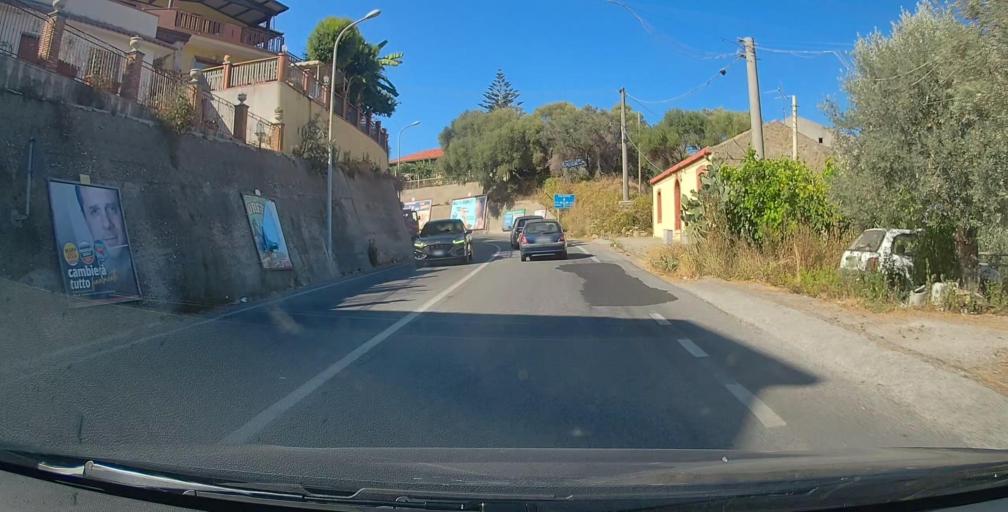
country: IT
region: Sicily
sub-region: Messina
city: Capo d'Orlando
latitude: 38.1552
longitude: 14.7521
